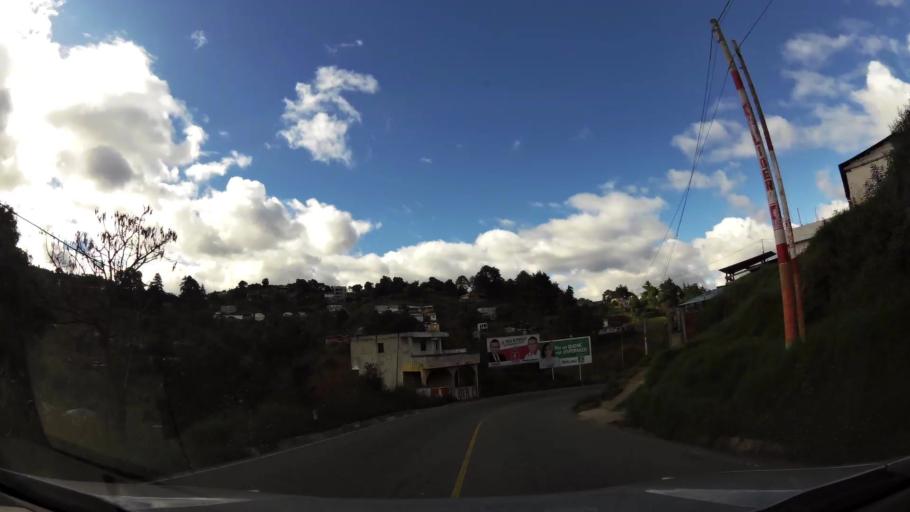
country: GT
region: Quiche
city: Chichicastenango
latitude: 14.9308
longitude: -91.1094
